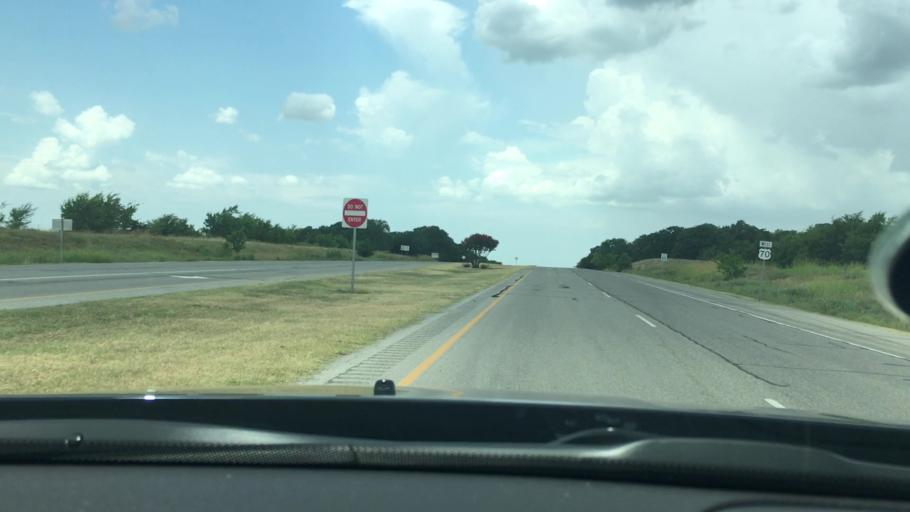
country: US
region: Oklahoma
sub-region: Carter County
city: Ardmore
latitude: 34.1394
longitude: -97.1435
